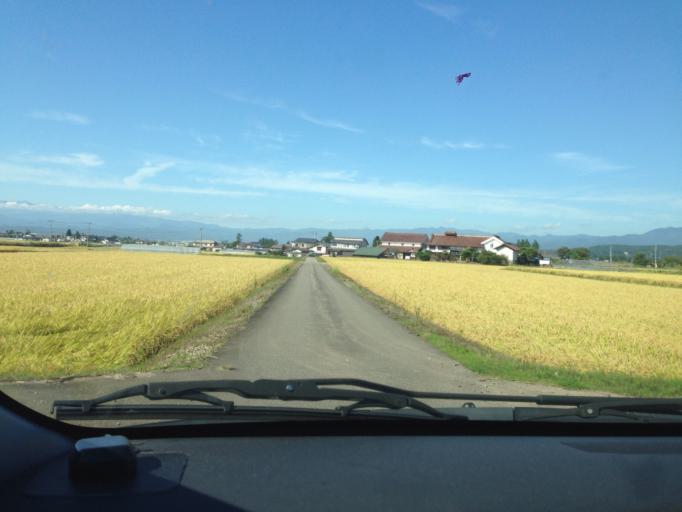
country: JP
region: Fukushima
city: Kitakata
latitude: 37.5454
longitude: 139.9171
